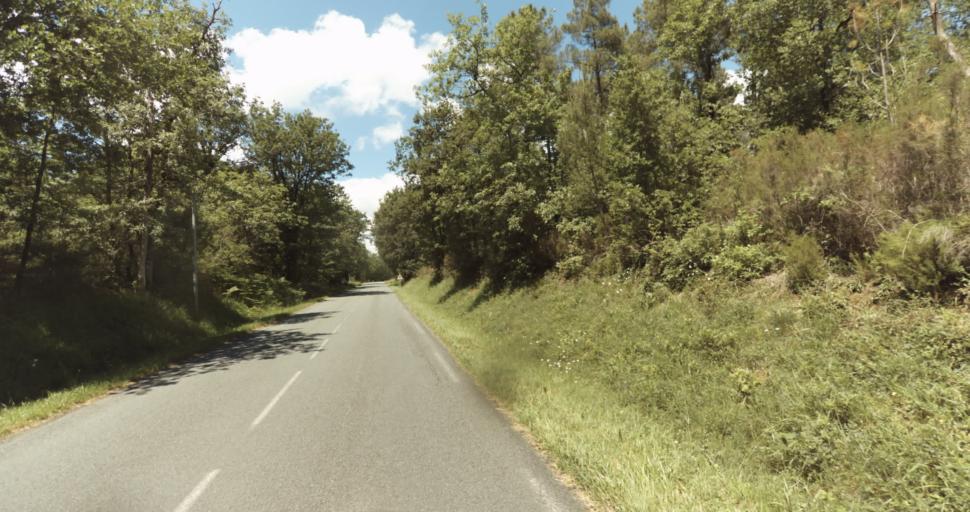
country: FR
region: Aquitaine
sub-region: Departement de la Dordogne
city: Beaumont-du-Perigord
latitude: 44.8029
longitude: 0.8509
